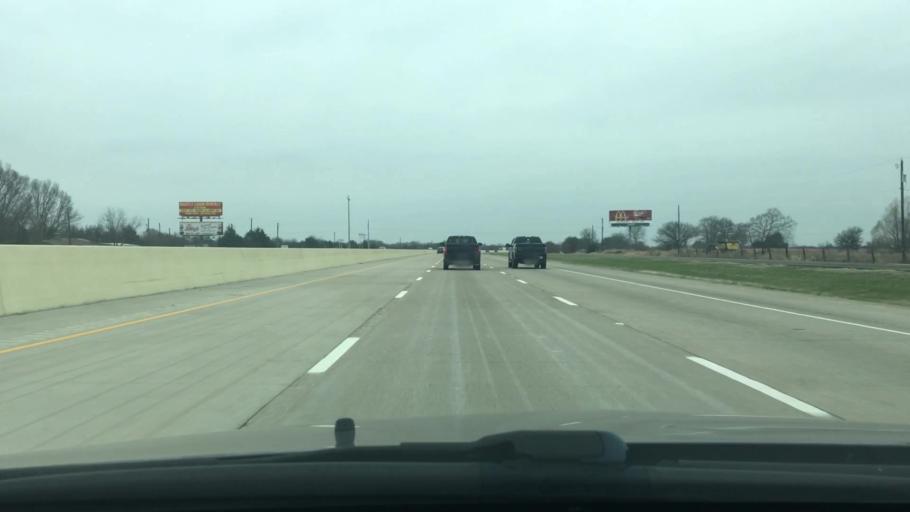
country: US
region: Texas
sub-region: Navarro County
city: Corsicana
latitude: 31.9894
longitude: -96.4260
